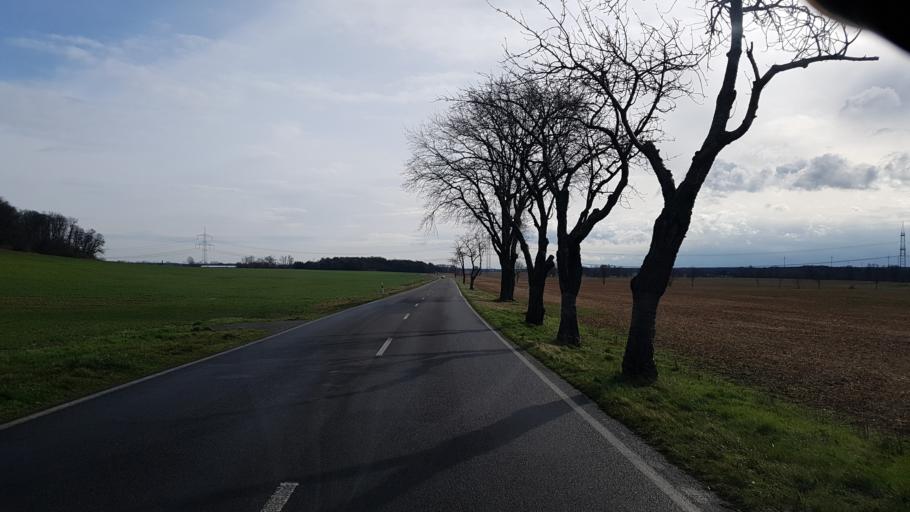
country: DE
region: Brandenburg
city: Schlieben
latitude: 51.7171
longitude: 13.3910
